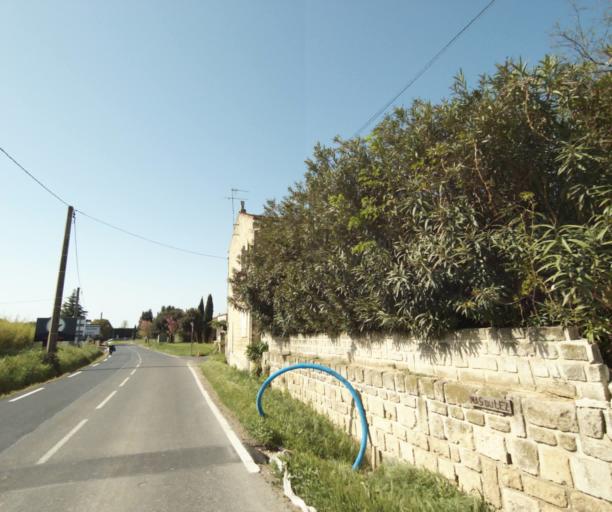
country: FR
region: Languedoc-Roussillon
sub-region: Departement de l'Herault
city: Lattes
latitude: 43.5801
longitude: 3.9082
